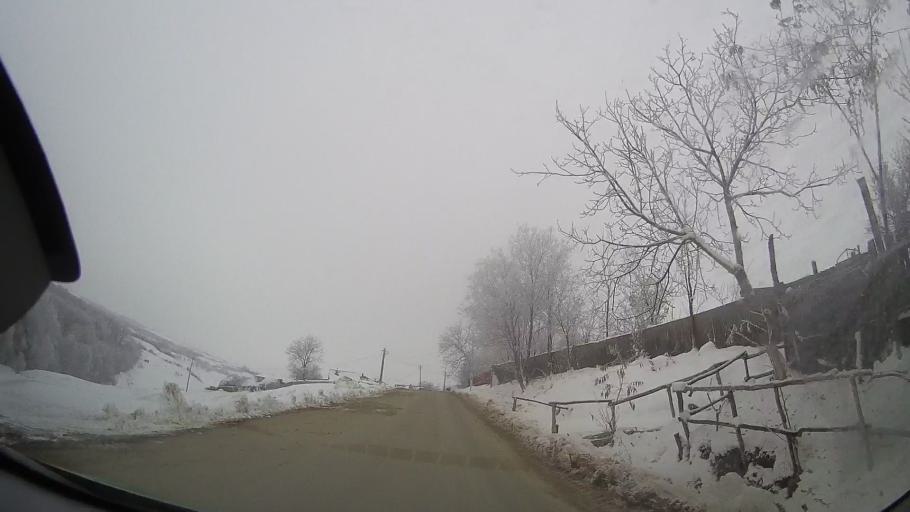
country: RO
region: Neamt
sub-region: Comuna Pancesti
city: Pancesti
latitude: 46.9107
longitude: 27.1590
